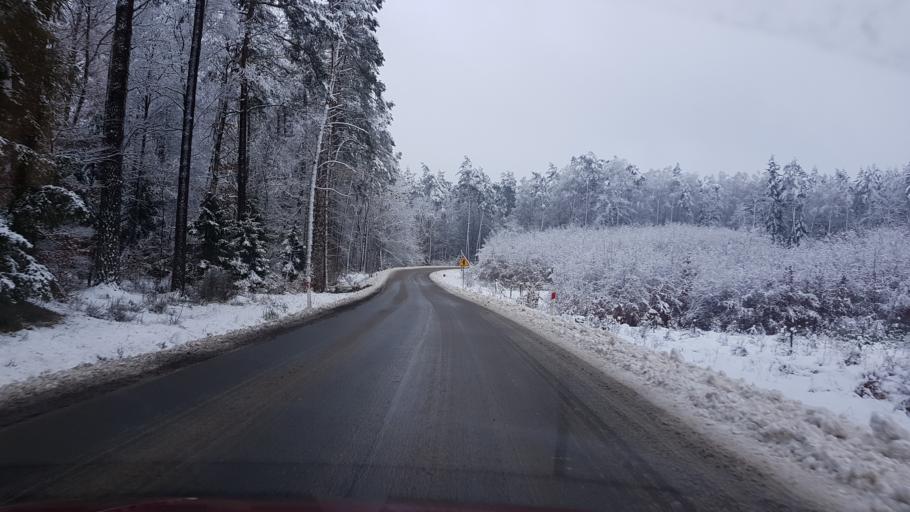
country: PL
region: West Pomeranian Voivodeship
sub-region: Powiat drawski
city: Zlocieniec
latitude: 53.5782
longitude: 16.0086
